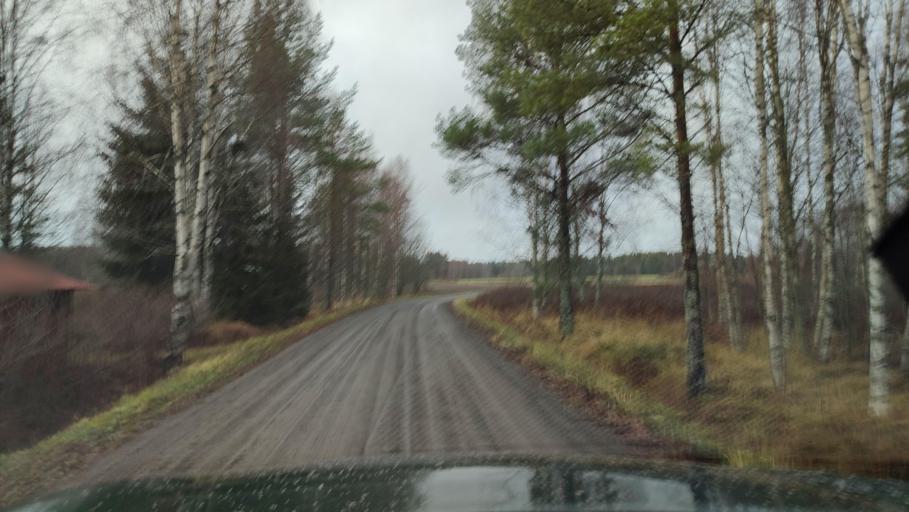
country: FI
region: Ostrobothnia
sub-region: Sydosterbotten
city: Naerpes
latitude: 62.4507
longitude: 21.5235
